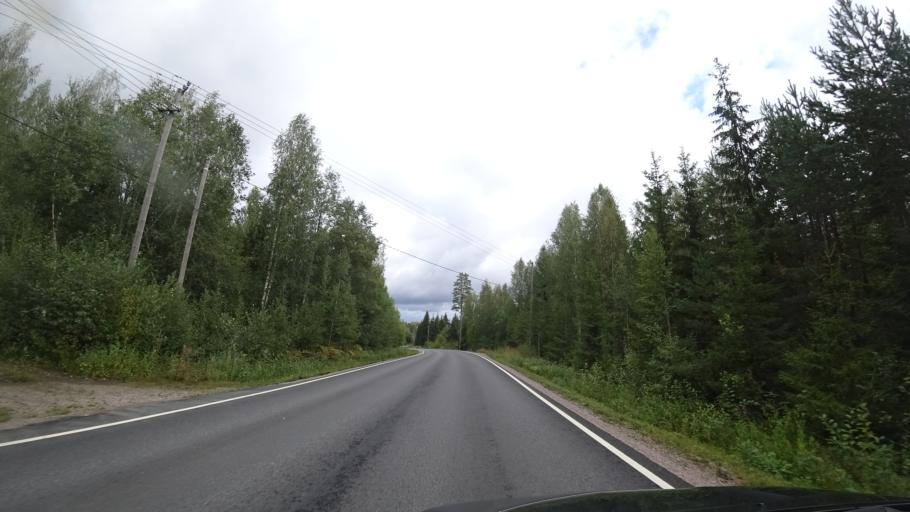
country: FI
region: Haeme
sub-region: Haemeenlinna
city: Lammi
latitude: 60.9719
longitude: 25.0118
